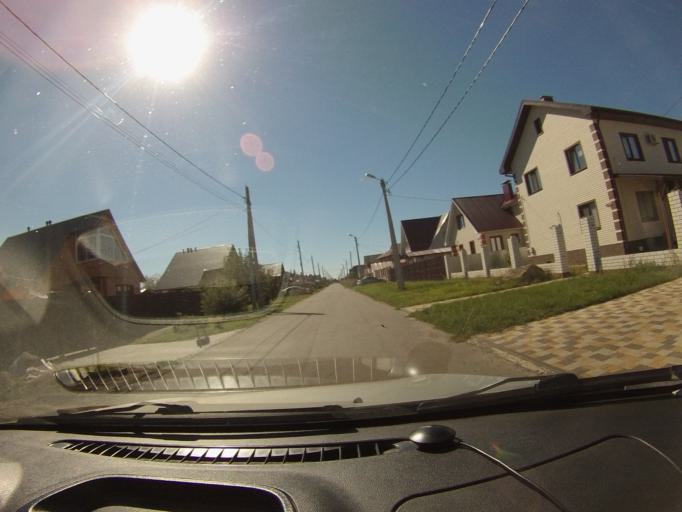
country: RU
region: Tambov
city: Tambov
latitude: 52.7750
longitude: 41.3806
